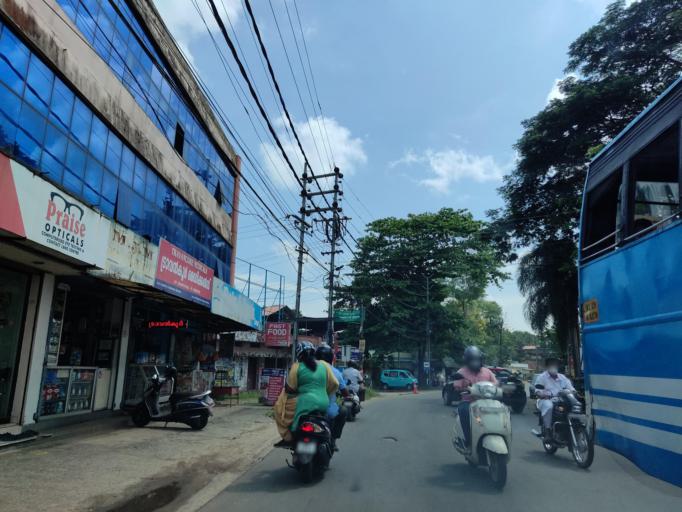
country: IN
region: Kerala
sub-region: Alappuzha
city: Mavelikara
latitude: 9.2548
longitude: 76.5516
